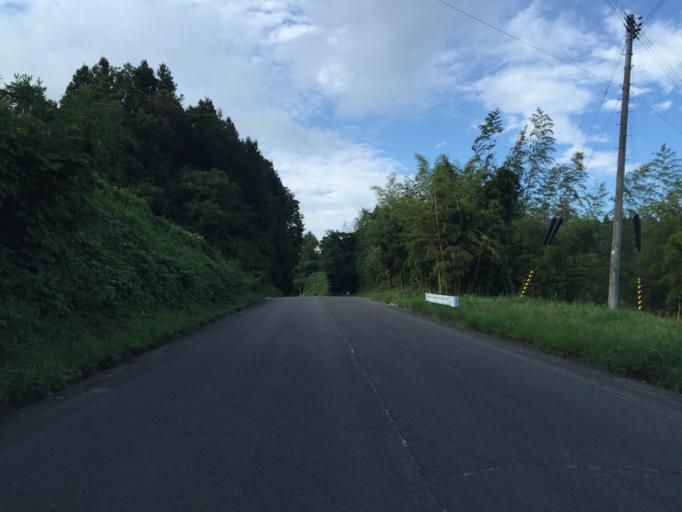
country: JP
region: Fukushima
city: Fukushima-shi
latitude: 37.6545
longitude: 140.5762
